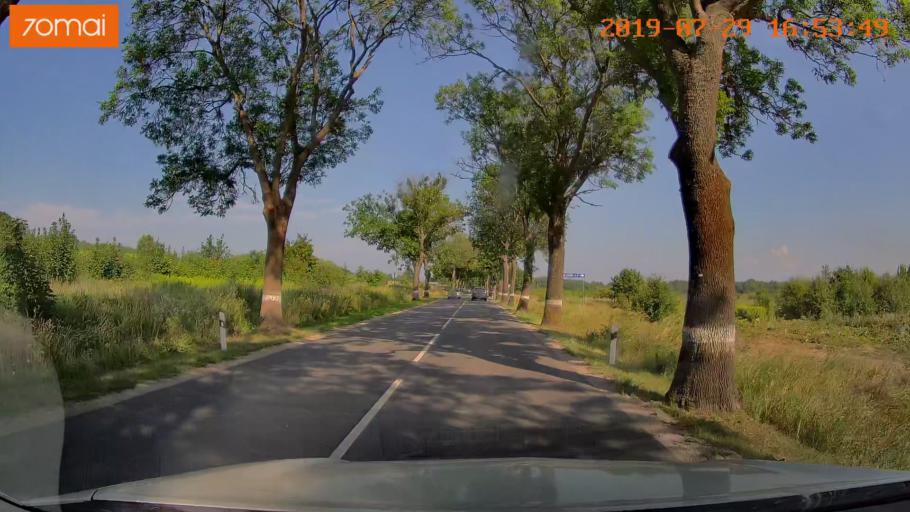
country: RU
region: Kaliningrad
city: Otradnoye
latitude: 54.8131
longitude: 20.1178
